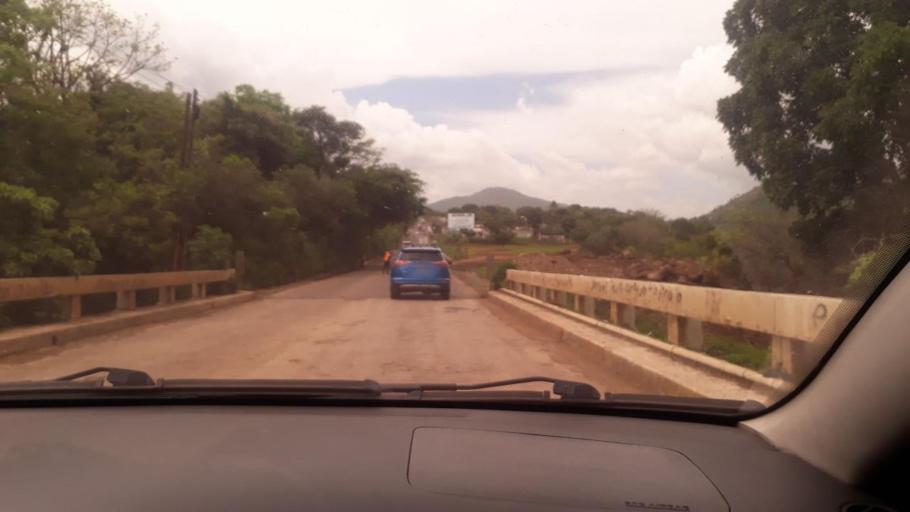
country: GT
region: Jutiapa
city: Quesada
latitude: 14.2468
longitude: -90.0292
